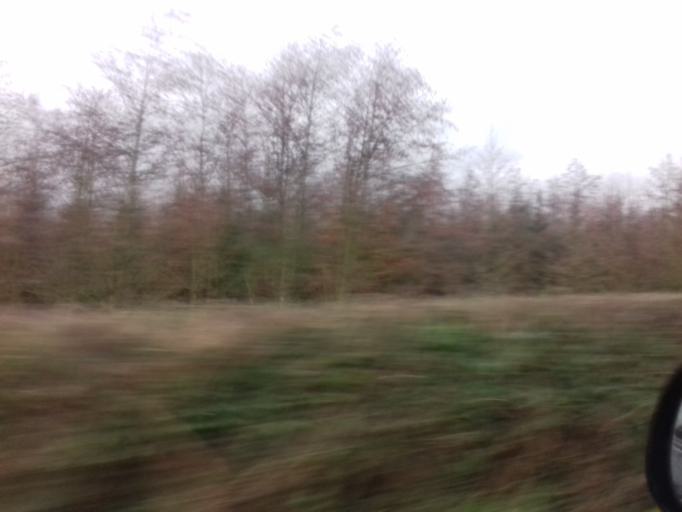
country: IE
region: Leinster
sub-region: Kilkenny
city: Graiguenamanagh
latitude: 52.5675
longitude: -6.9526
